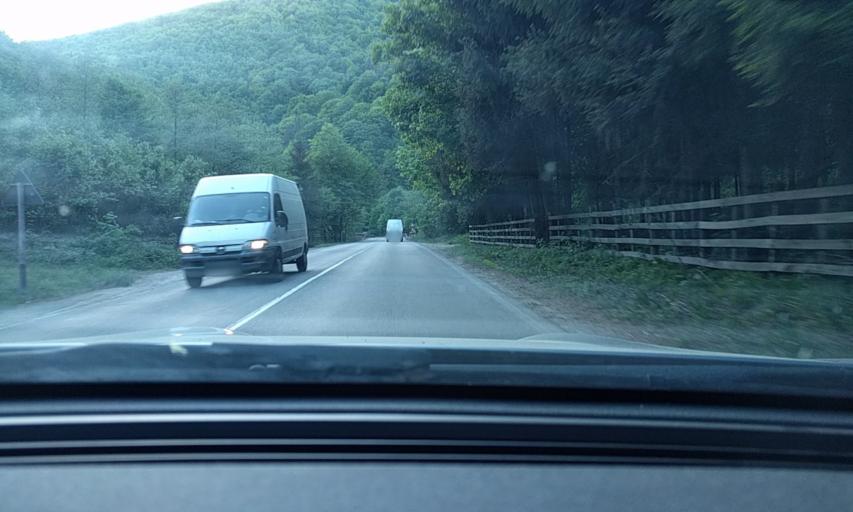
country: RO
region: Bacau
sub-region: Oras Slanic-Moldova
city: Slanic-Moldova
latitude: 46.1199
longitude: 26.4280
